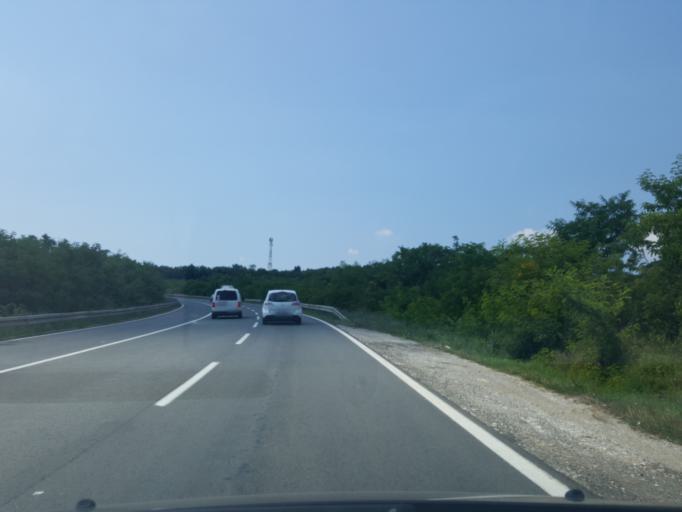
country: RS
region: Central Serbia
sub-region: Belgrade
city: Sopot
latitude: 44.5464
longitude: 20.6592
